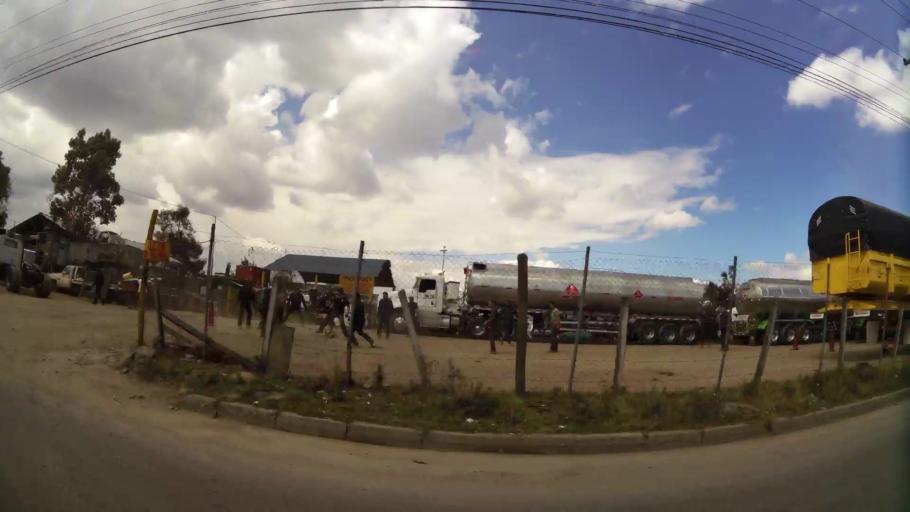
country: CO
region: Bogota D.C.
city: Bogota
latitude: 4.6353
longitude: -74.1051
